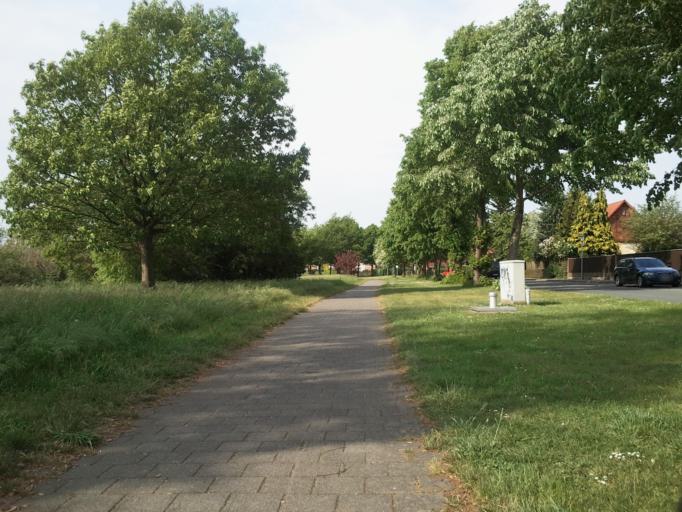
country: DE
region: Lower Saxony
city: Nienburg
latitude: 52.6278
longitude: 9.2094
